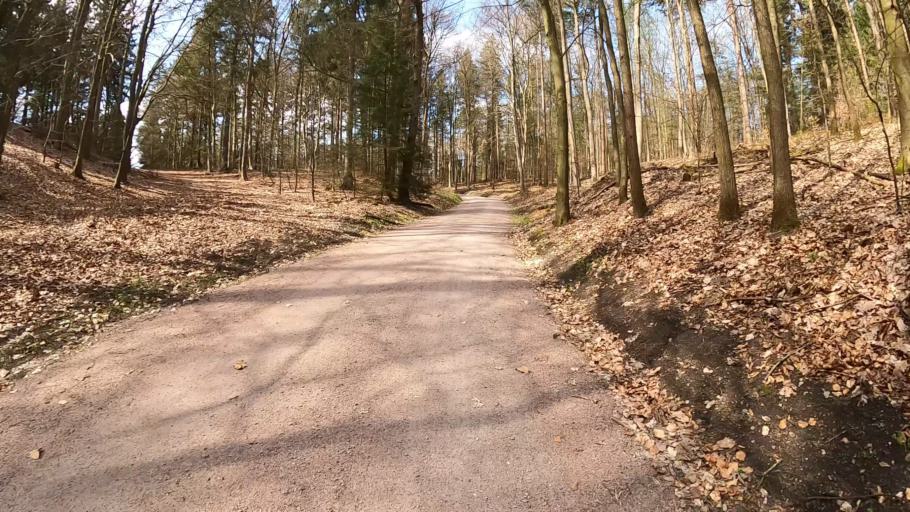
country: DE
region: Hamburg
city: Harburg
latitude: 53.4616
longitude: 9.9111
